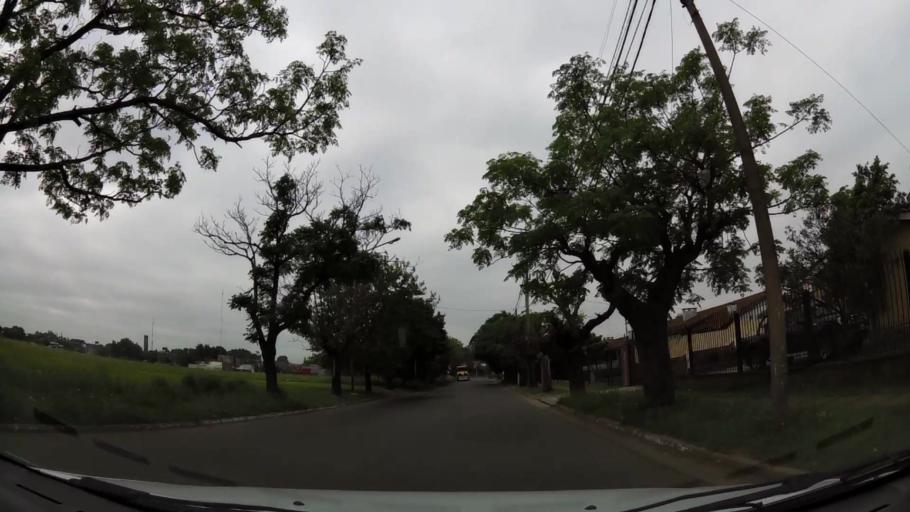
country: AR
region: Buenos Aires
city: San Justo
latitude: -34.7078
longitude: -58.5415
